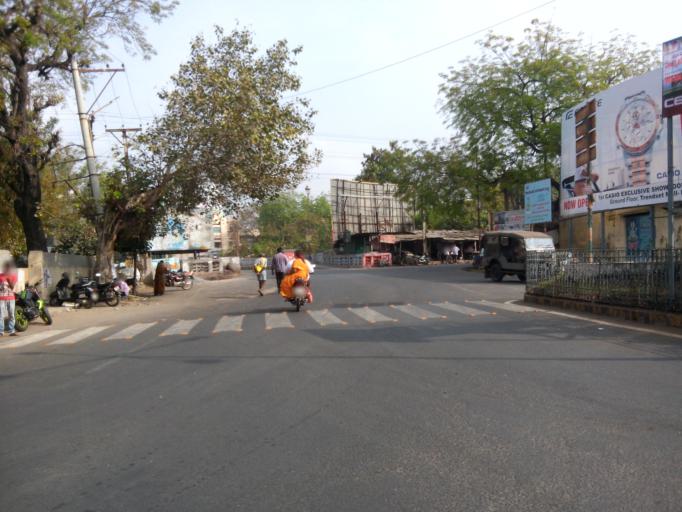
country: IN
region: Andhra Pradesh
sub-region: Krishna
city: Vijayawada
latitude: 16.5131
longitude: 80.6230
